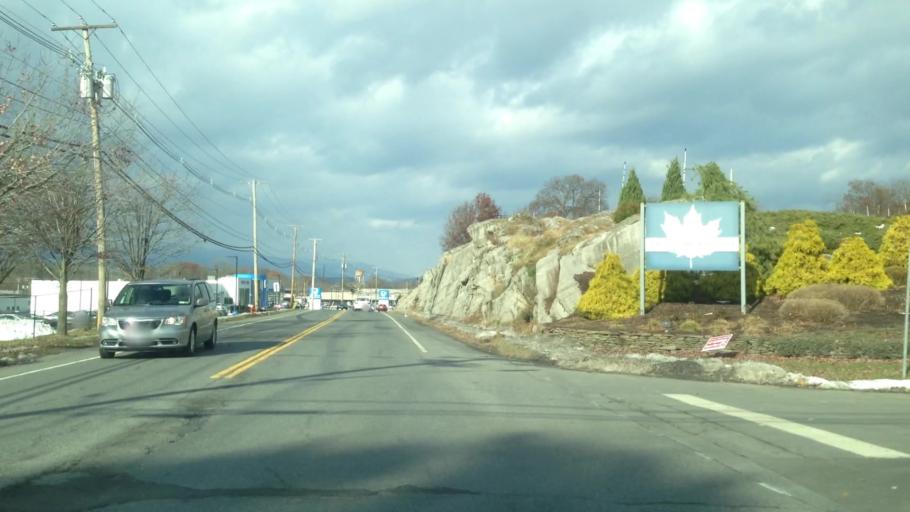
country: US
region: New York
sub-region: Ulster County
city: Lincoln Park
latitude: 41.9538
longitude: -73.9909
